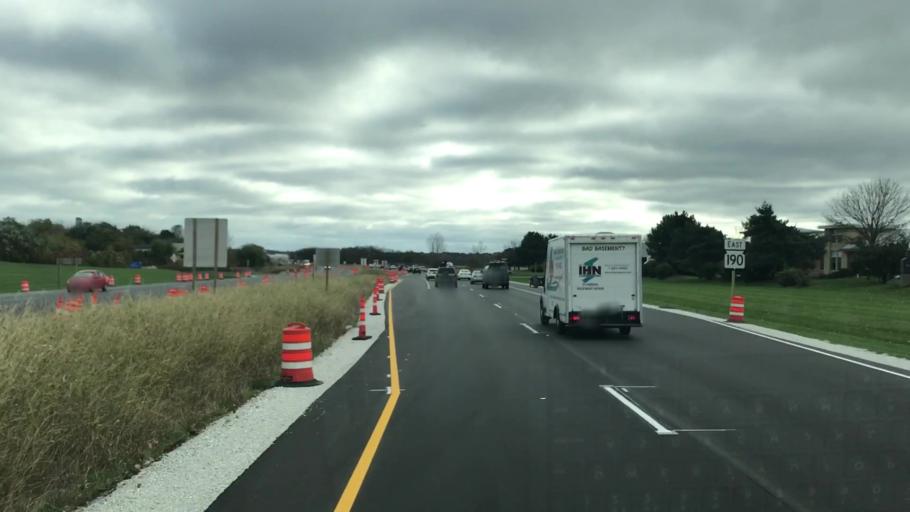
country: US
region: Wisconsin
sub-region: Waukesha County
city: Sussex
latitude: 43.0825
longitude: -88.1833
